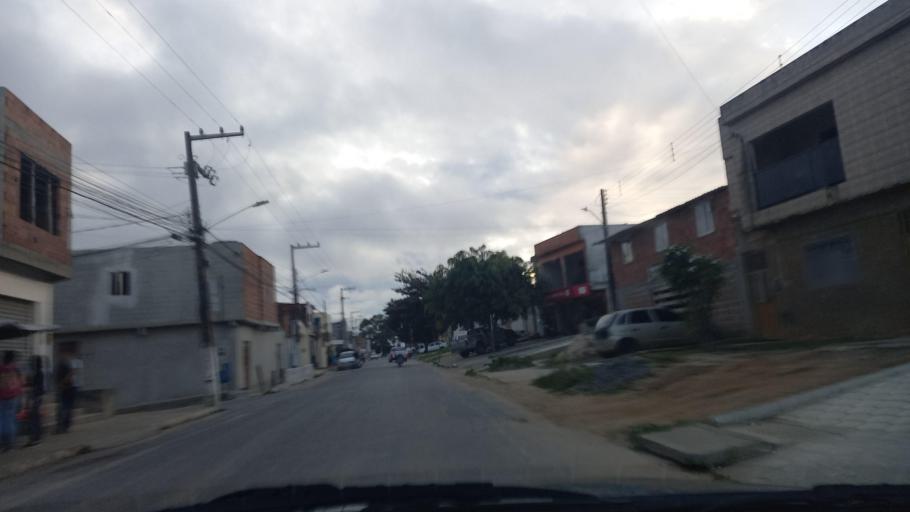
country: BR
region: Pernambuco
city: Garanhuns
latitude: -8.8899
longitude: -36.4569
